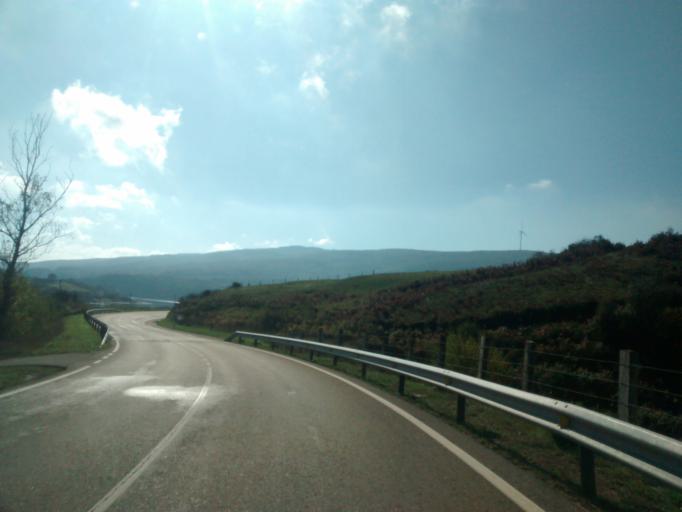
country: ES
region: Cantabria
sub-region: Provincia de Cantabria
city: Reinosa
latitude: 42.9846
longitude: -4.1064
